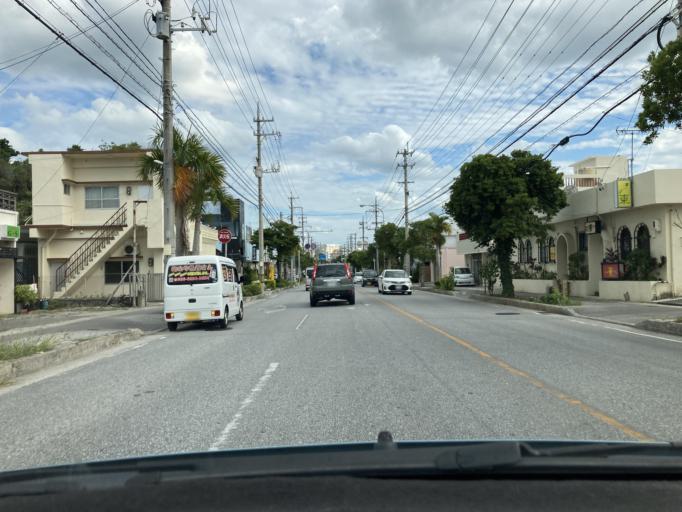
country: JP
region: Okinawa
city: Okinawa
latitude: 26.3576
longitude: 127.8268
